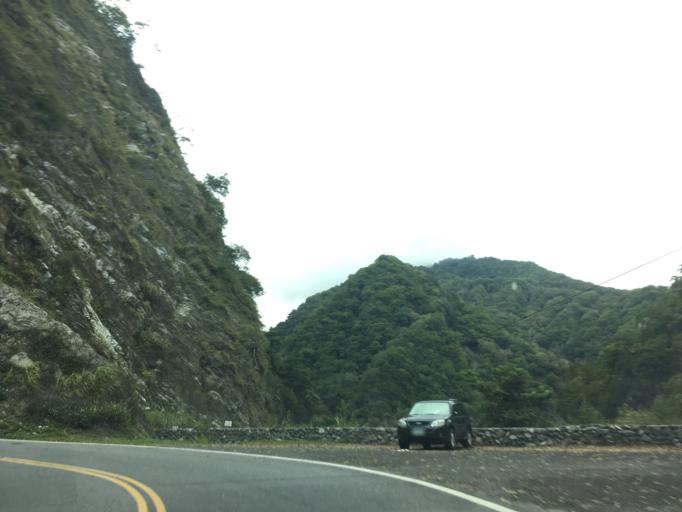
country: TW
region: Taiwan
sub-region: Hualien
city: Hualian
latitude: 24.2146
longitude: 121.4836
